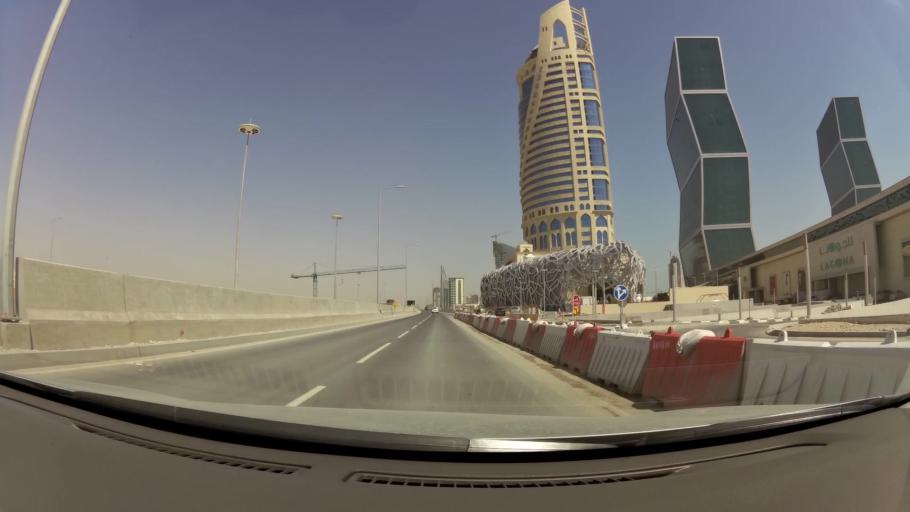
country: QA
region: Baladiyat ad Dawhah
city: Doha
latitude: 25.3756
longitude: 51.5234
